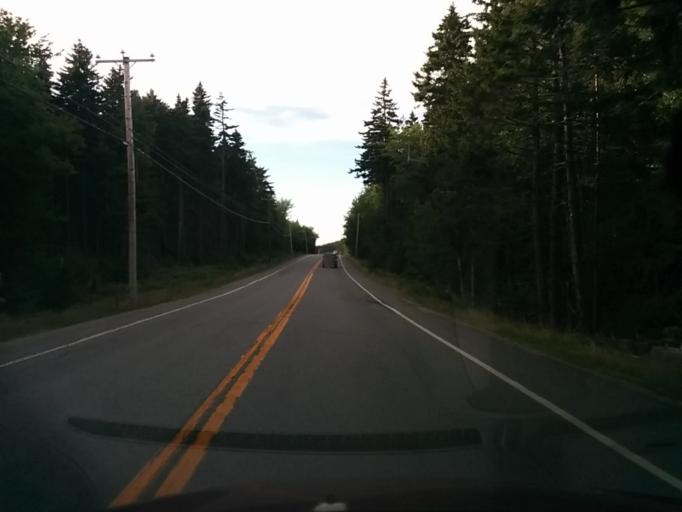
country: US
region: Maine
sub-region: Hancock County
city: Tremont
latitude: 44.3137
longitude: -68.2861
